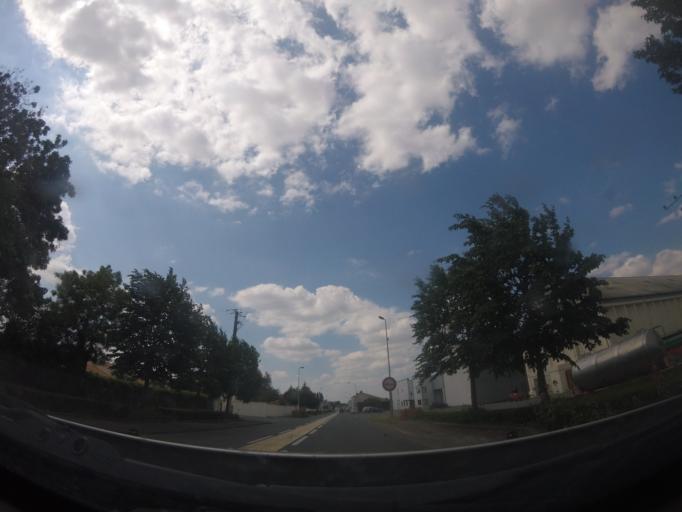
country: FR
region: Poitou-Charentes
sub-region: Departement de la Charente-Maritime
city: Bords
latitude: 45.8572
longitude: -0.8316
